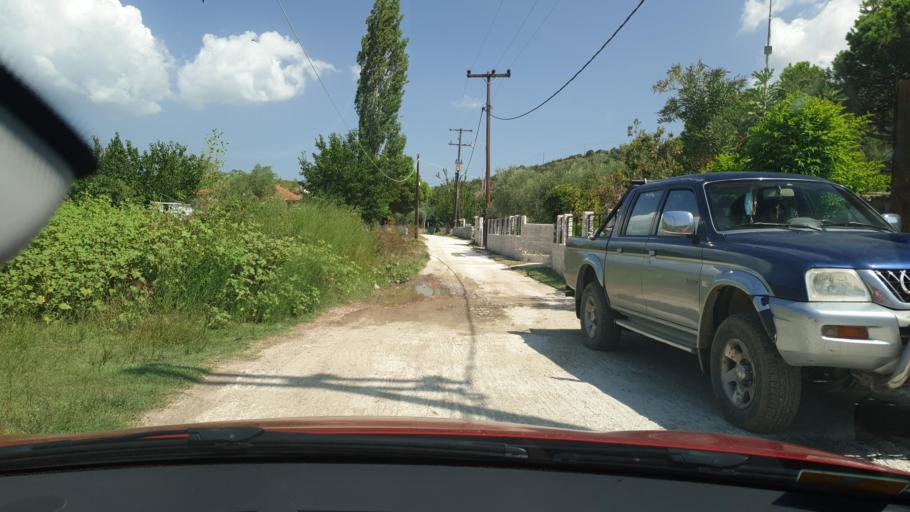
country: GR
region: Central Macedonia
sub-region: Nomos Chalkidikis
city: Sykia
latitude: 39.9798
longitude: 23.9085
